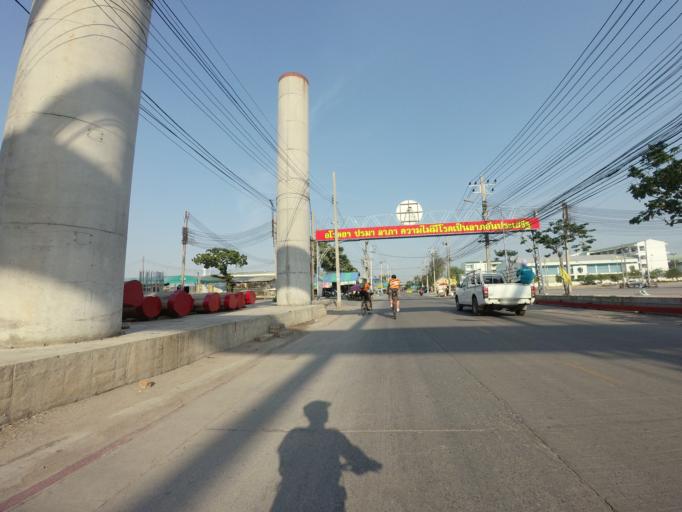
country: TH
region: Samut Sakhon
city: Samut Sakhon
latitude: 13.5311
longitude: 100.2754
